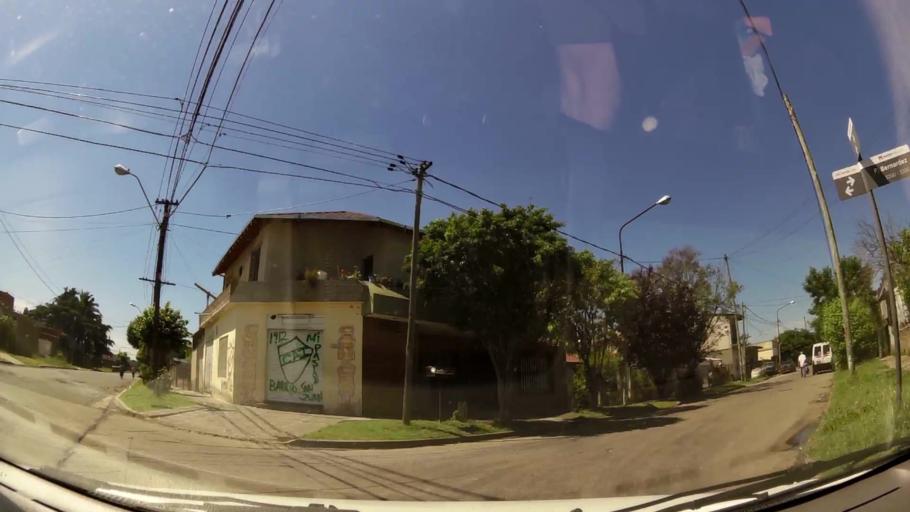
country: AR
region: Buenos Aires
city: Ituzaingo
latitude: -34.6829
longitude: -58.6569
